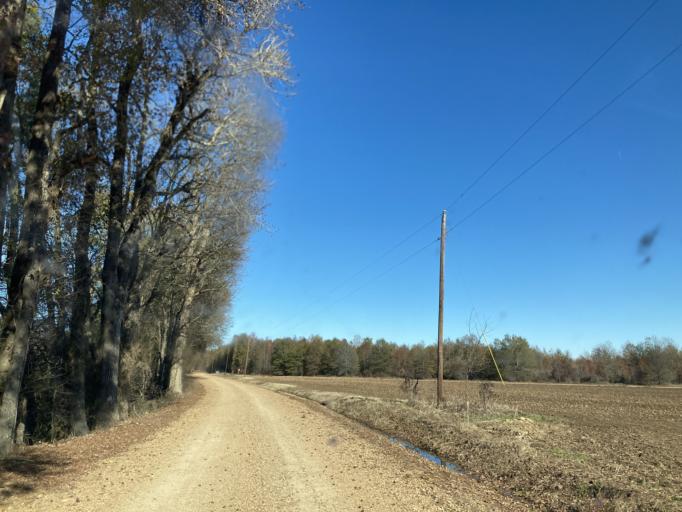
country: US
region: Mississippi
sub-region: Sharkey County
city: Rolling Fork
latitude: 32.7538
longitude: -90.6919
